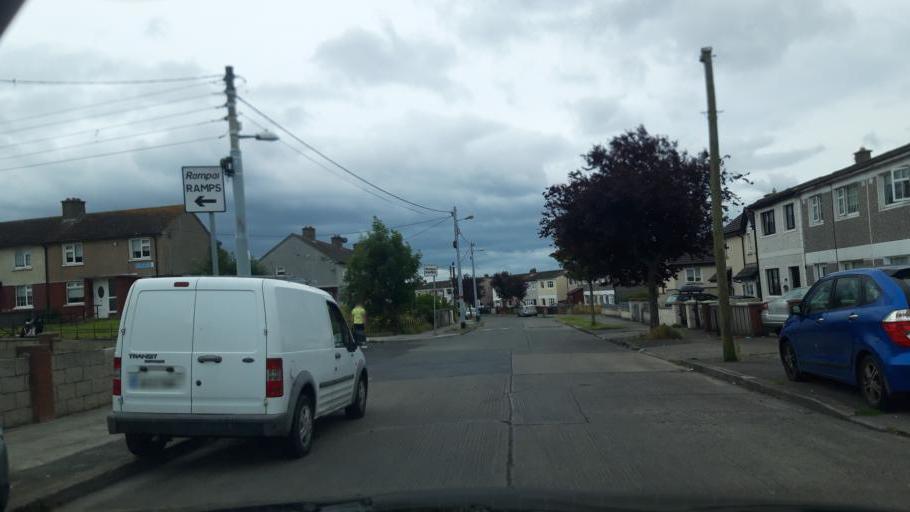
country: IE
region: Leinster
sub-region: Dublin City
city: Finglas
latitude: 53.3828
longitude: -6.3090
